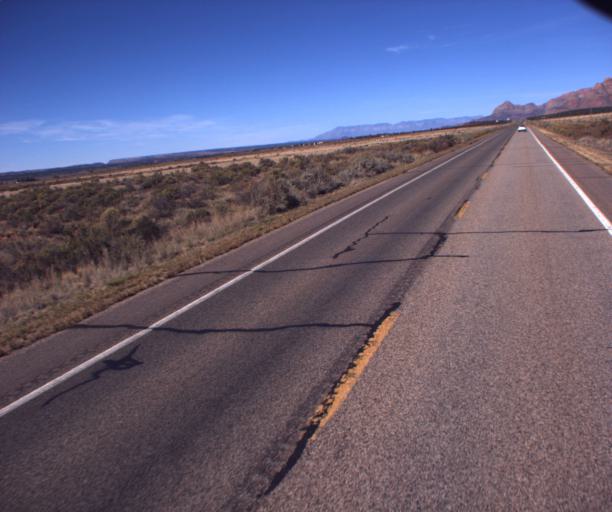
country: US
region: Arizona
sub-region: Mohave County
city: Colorado City
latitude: 36.9360
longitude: -112.9475
